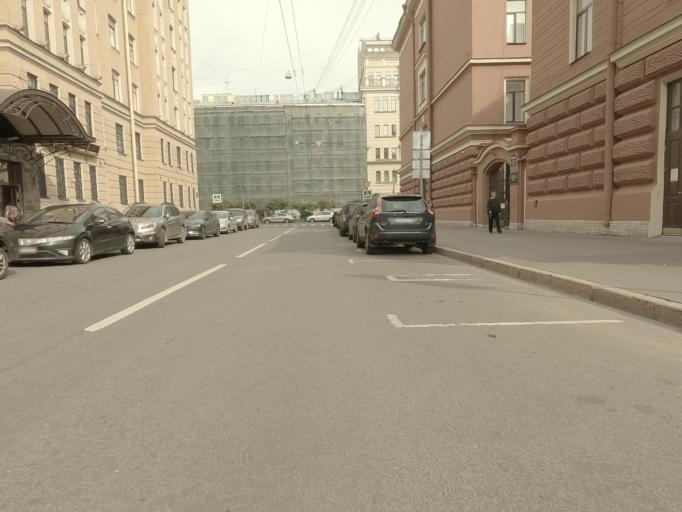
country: RU
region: St.-Petersburg
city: Admiralteisky
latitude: 59.9121
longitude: 30.2914
